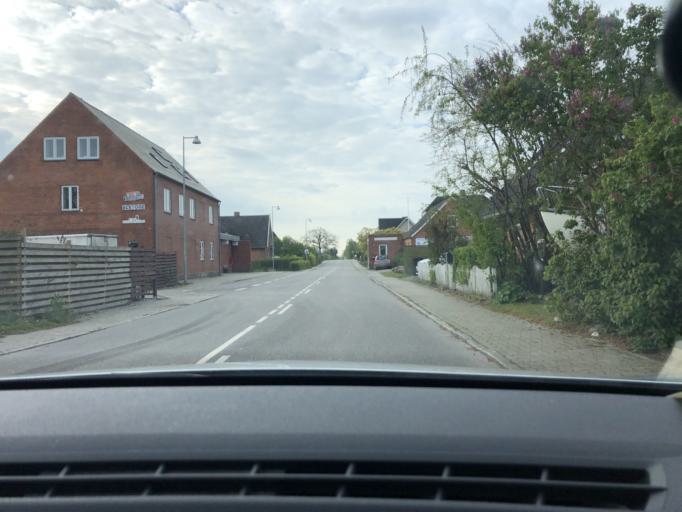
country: DK
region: Zealand
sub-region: Faxe Kommune
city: Ronnede
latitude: 55.2448
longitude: 12.0404
